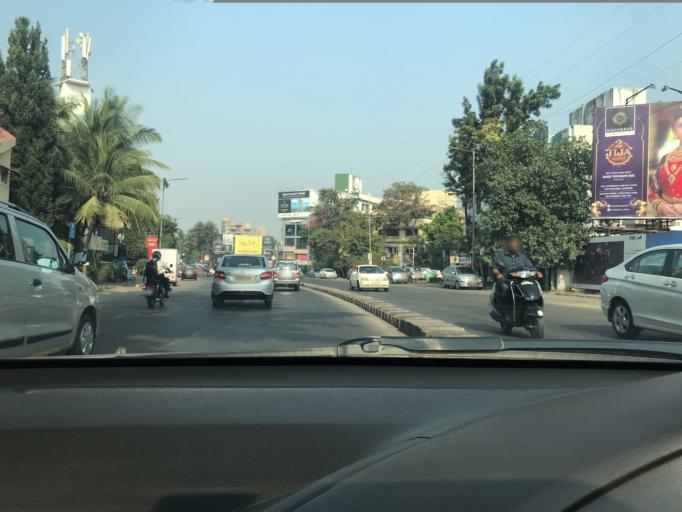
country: IN
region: Maharashtra
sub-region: Pune Division
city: Khadki
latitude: 18.5535
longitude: 73.8025
